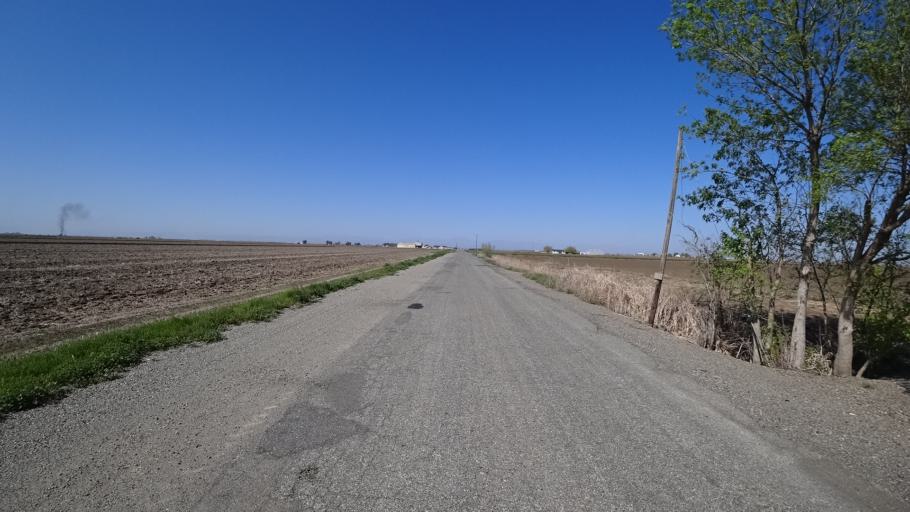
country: US
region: California
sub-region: Glenn County
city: Willows
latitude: 39.4283
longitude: -122.0256
